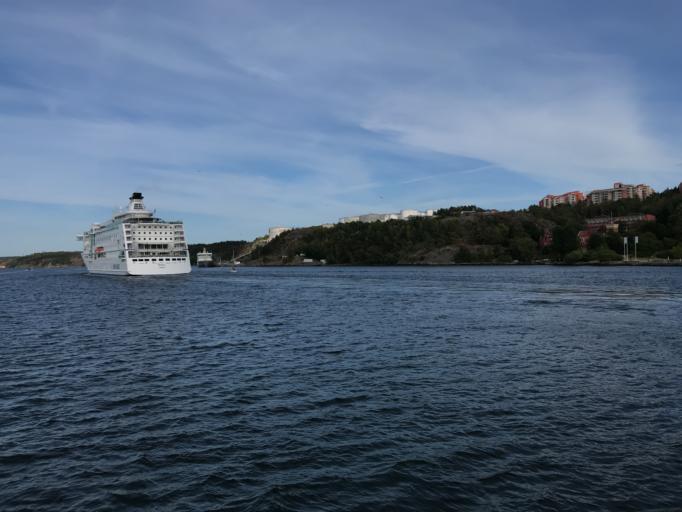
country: SE
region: Stockholm
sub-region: Nacka Kommun
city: Nacka
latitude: 59.3205
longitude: 18.1576
